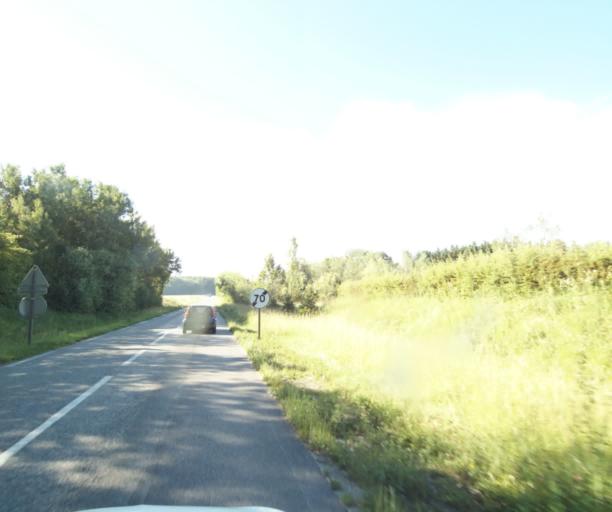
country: FR
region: Rhone-Alpes
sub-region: Departement de la Haute-Savoie
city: Douvaine
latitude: 46.3224
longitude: 6.2945
